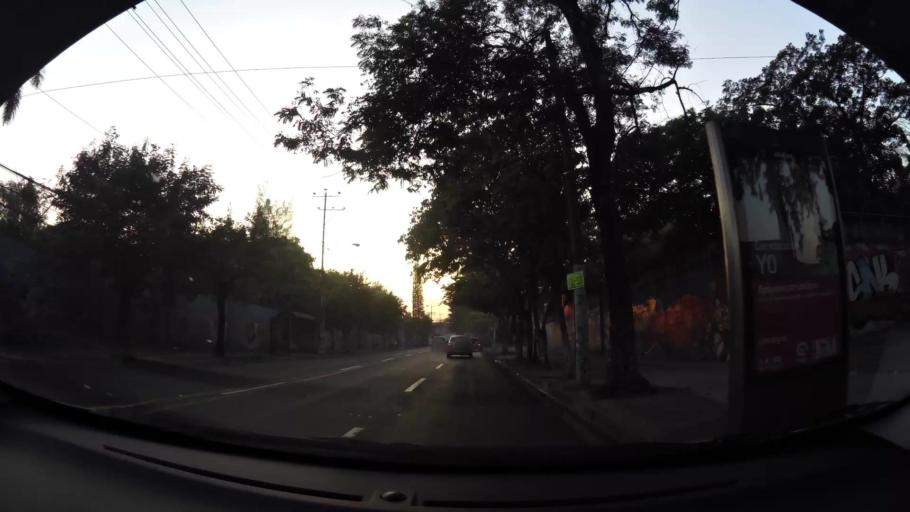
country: SV
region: San Salvador
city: Mejicanos
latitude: 13.7151
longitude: -89.2055
